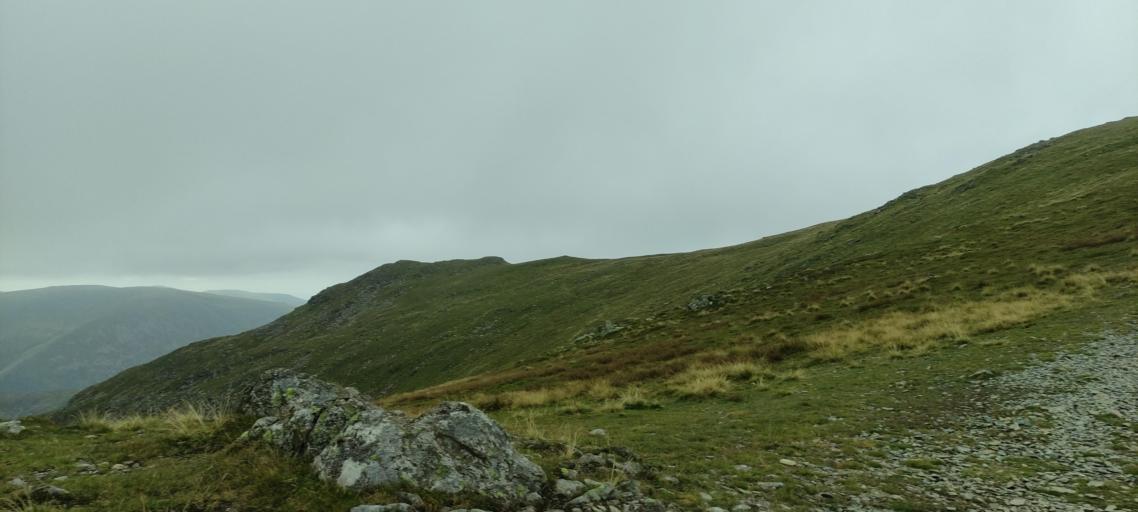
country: GB
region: England
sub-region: Cumbria
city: Ambleside
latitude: 54.5161
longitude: -2.9737
